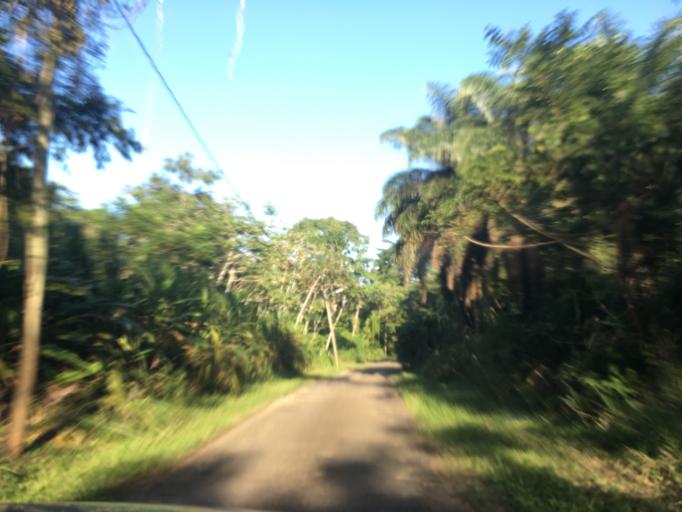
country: BZ
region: Stann Creek
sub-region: Dangriga
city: Dangriga
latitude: 16.8243
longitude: -88.3141
